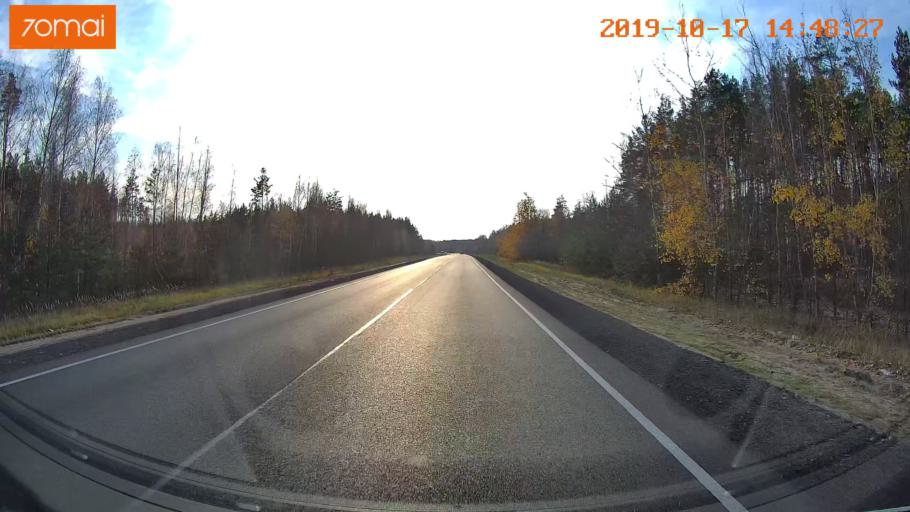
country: RU
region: Rjazan
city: Solotcha
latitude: 54.7587
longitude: 39.8455
